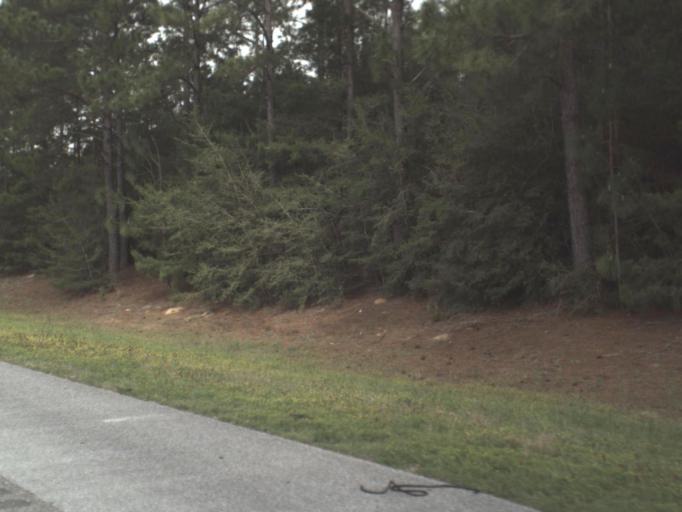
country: US
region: Florida
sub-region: Okaloosa County
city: Crestview
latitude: 30.7269
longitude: -86.4991
